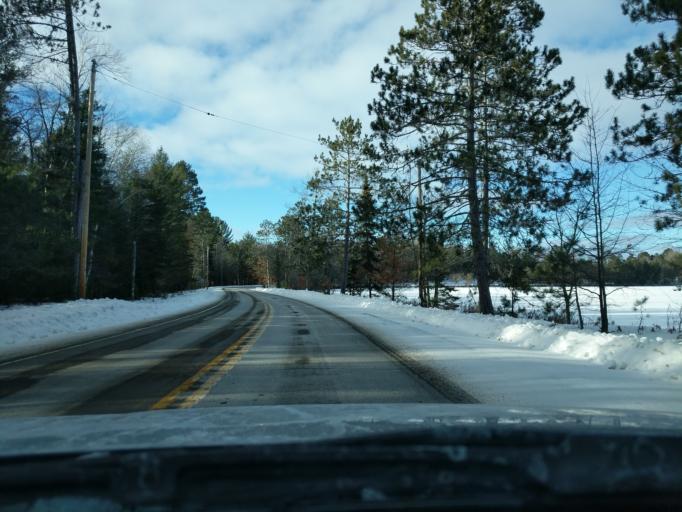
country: US
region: Wisconsin
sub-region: Vilas County
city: Eagle River
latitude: 45.7738
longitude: -89.0733
